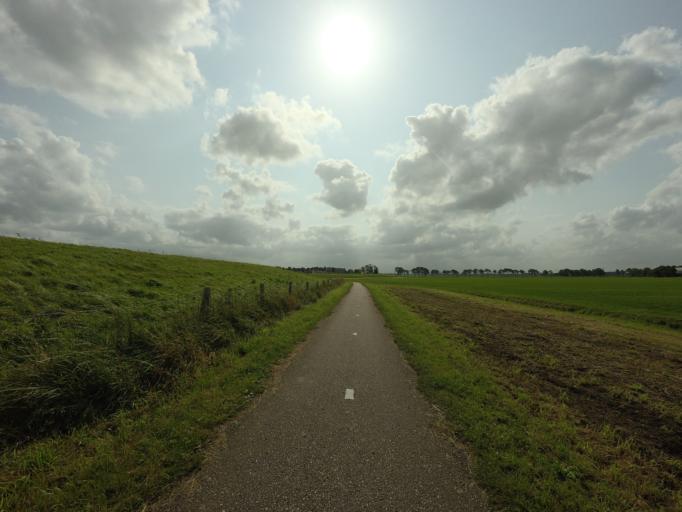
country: NL
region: North Holland
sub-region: Gemeente Waterland
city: Broek in Waterland
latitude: 52.4294
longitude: 4.9947
